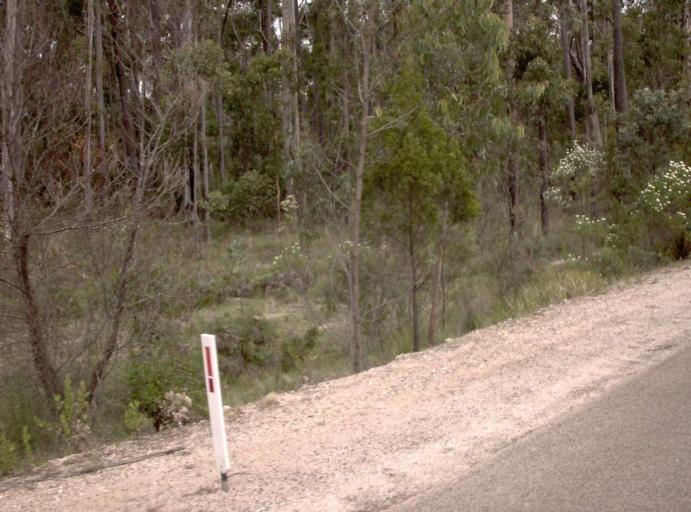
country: AU
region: Victoria
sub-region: East Gippsland
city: Lakes Entrance
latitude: -37.7137
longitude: 148.0745
